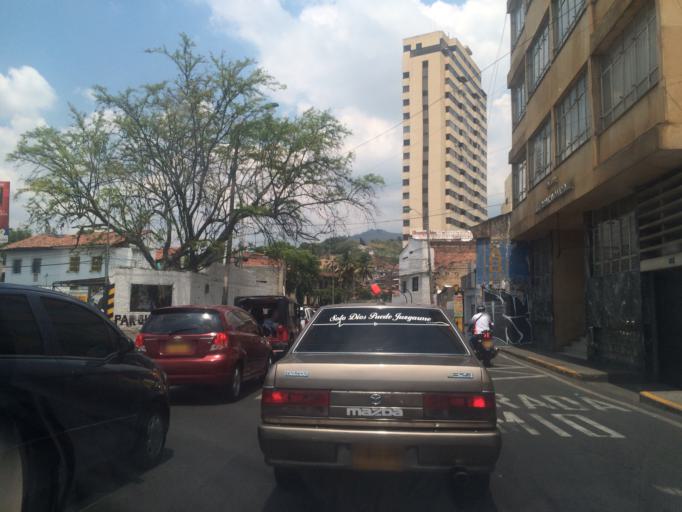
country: CO
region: Valle del Cauca
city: Cali
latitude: 3.4497
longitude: -76.5378
